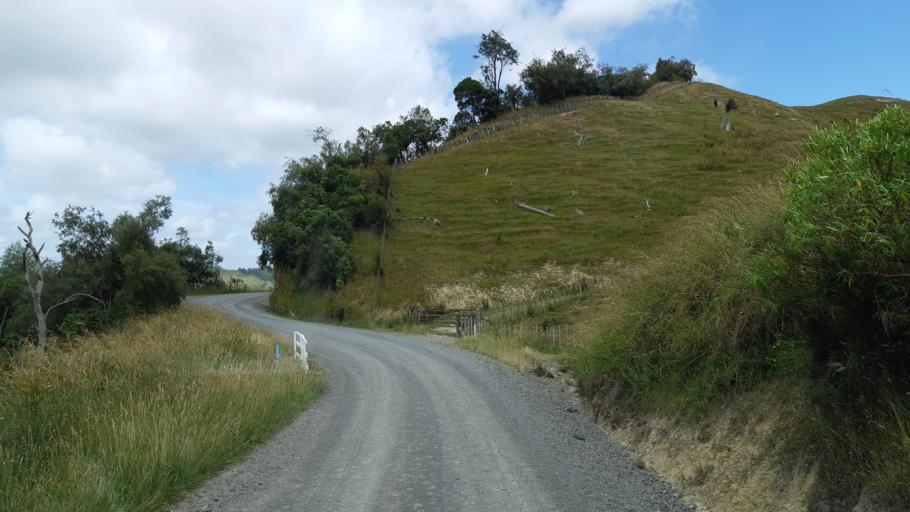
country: NZ
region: Manawatu-Wanganui
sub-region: Ruapehu District
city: Waiouru
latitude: -39.7805
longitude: 175.9093
